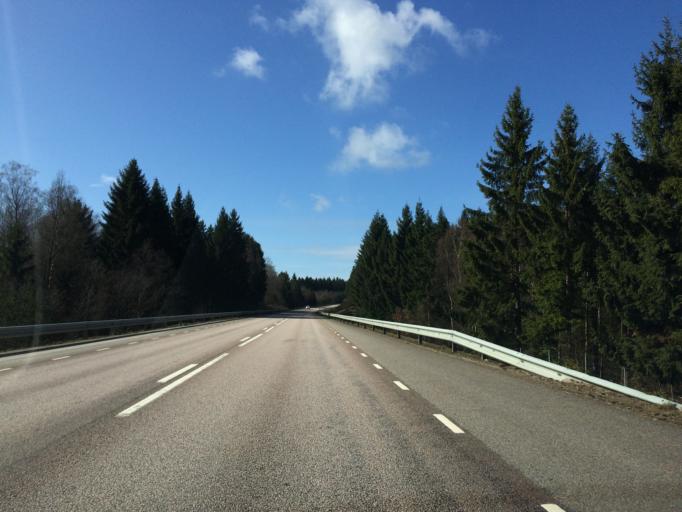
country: SE
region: Halland
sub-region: Laholms Kommun
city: Knared
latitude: 56.5221
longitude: 13.2622
